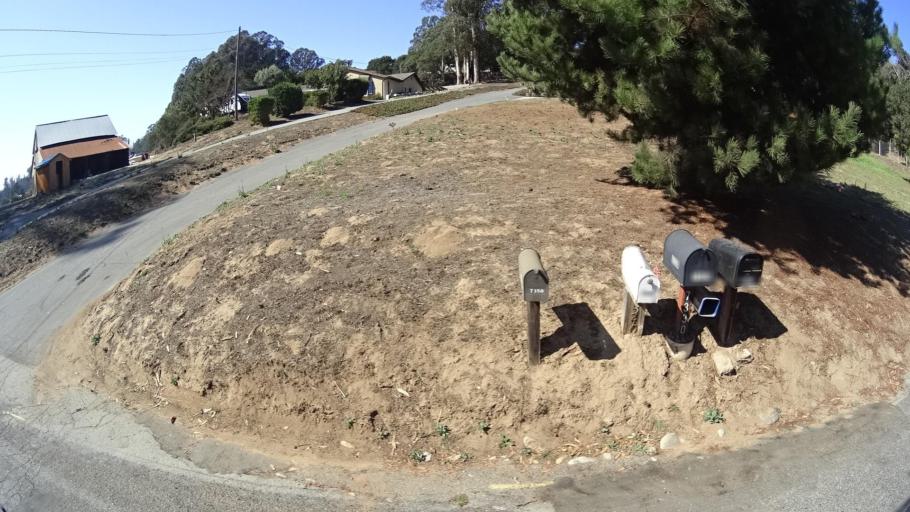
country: US
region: California
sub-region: Monterey County
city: Prunedale
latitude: 36.8108
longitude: -121.6564
